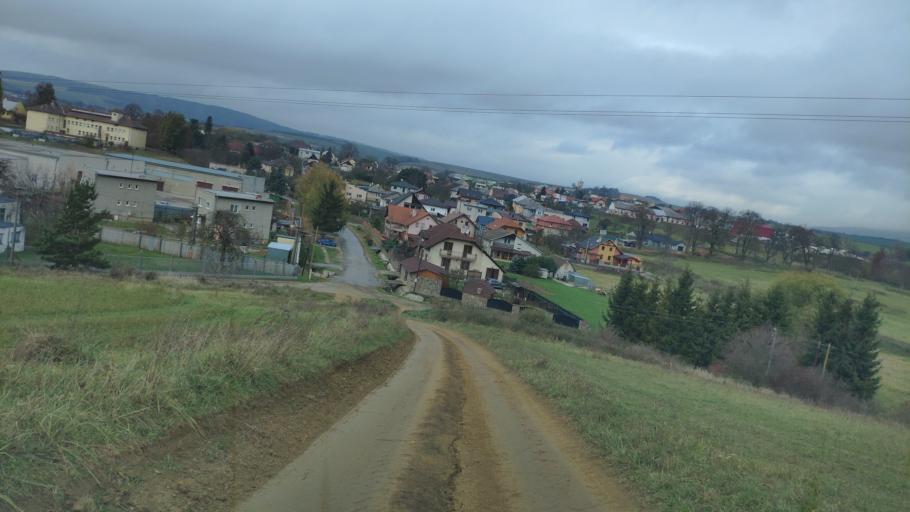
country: SK
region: Presovsky
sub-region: Okres Presov
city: Presov
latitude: 49.0112
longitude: 21.1915
